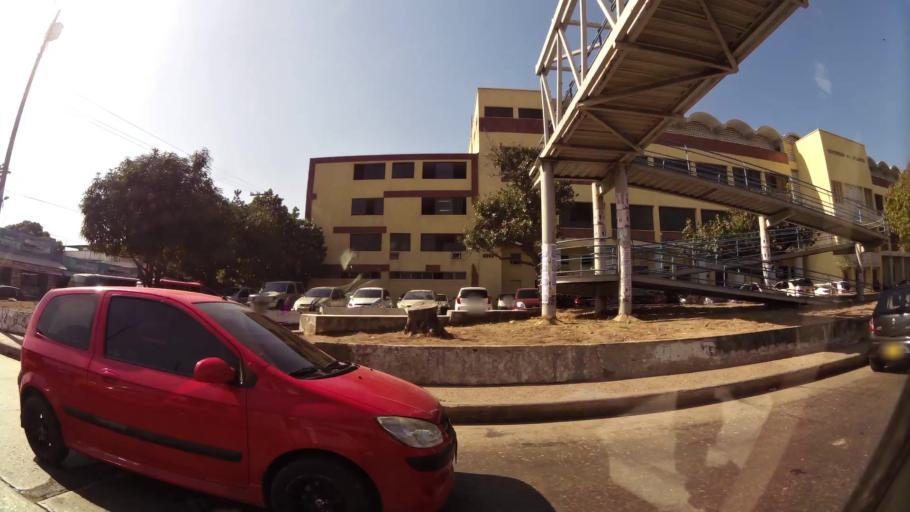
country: CO
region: Atlantico
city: Barranquilla
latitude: 10.9838
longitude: -74.7896
